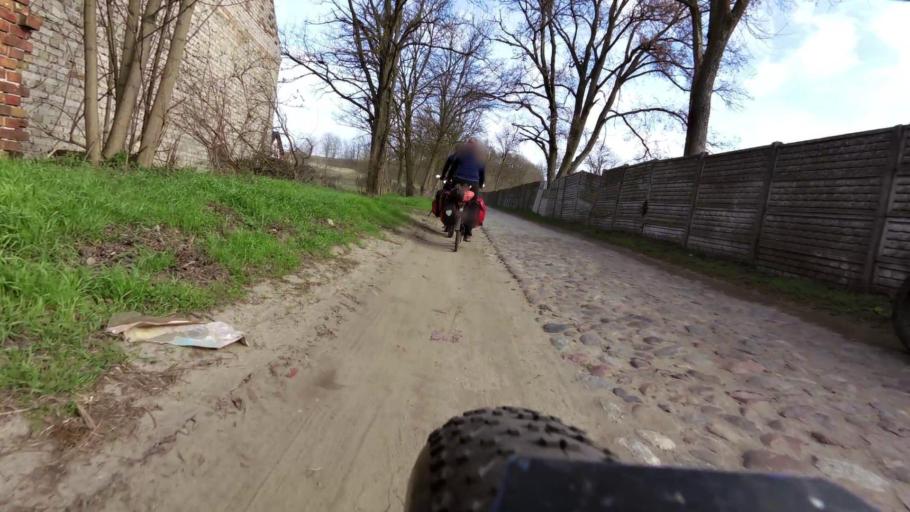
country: DE
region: Brandenburg
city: Brieskow-Finkenheerd
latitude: 52.2845
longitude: 14.6175
